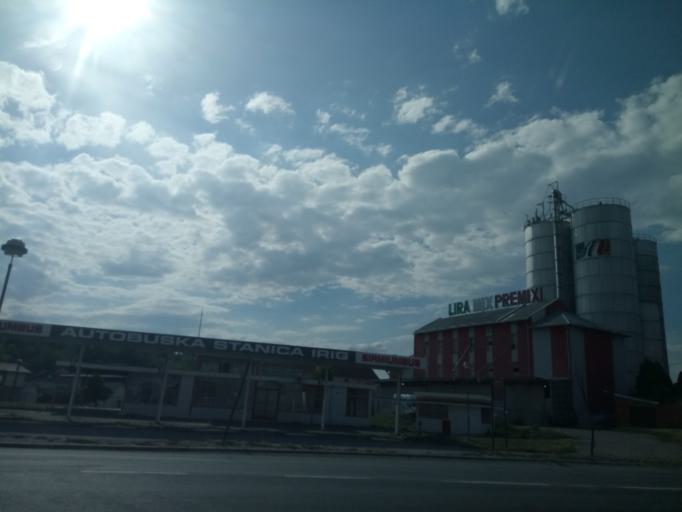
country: RS
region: Autonomna Pokrajina Vojvodina
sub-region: Sremski Okrug
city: Irig
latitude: 45.0927
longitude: 19.8624
